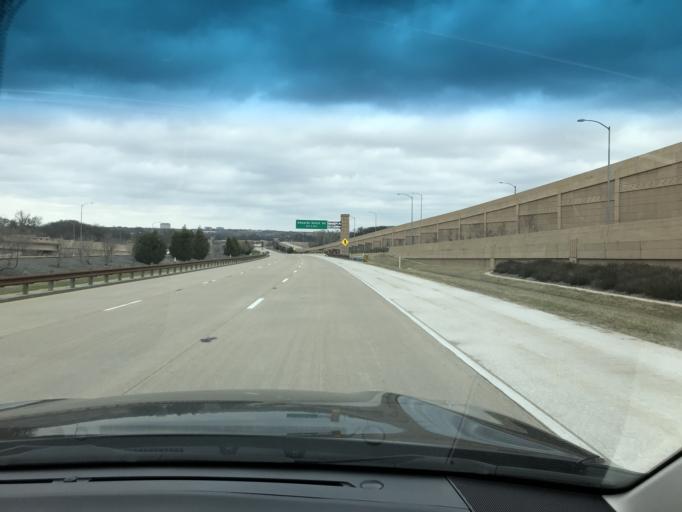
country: US
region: Texas
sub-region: Tarrant County
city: Benbrook
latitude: 32.6922
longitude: -97.4043
